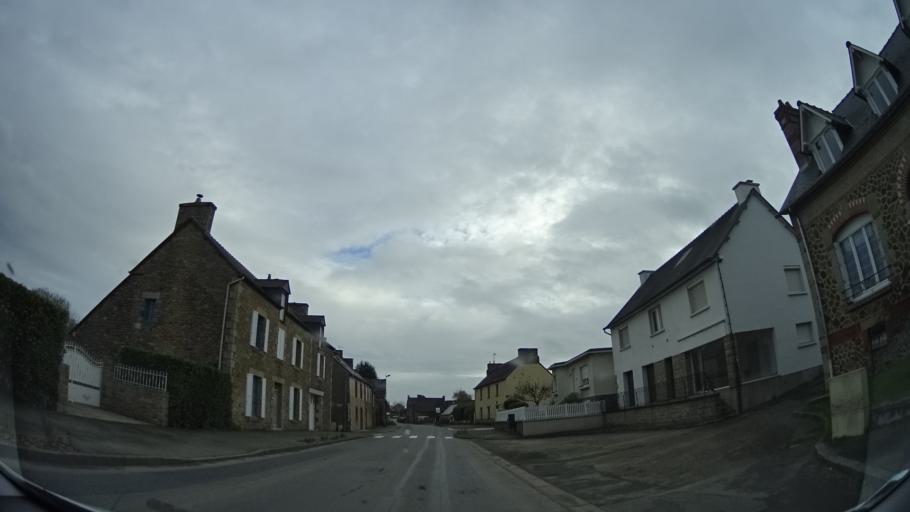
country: FR
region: Brittany
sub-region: Departement des Cotes-d'Armor
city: Evran
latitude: 48.3790
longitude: -1.9776
